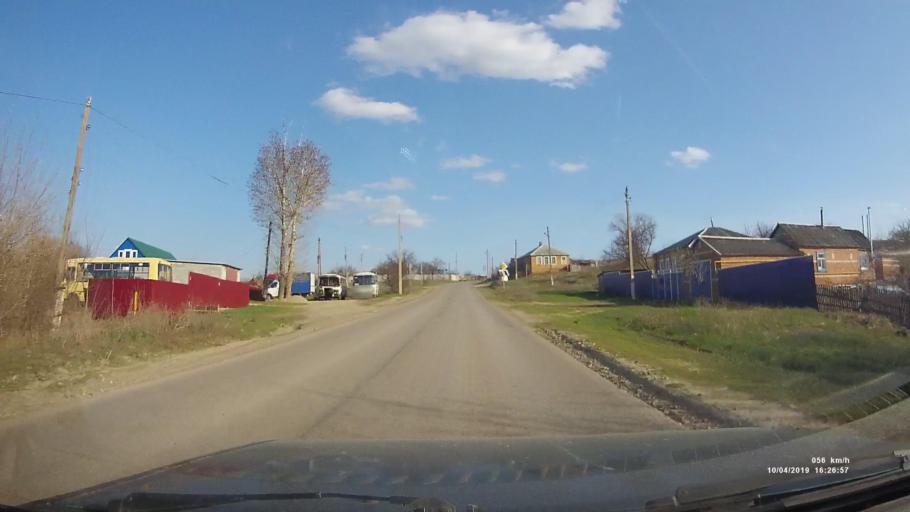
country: RU
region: Rostov
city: Staraya Stanitsa
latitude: 48.2875
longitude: 40.3405
